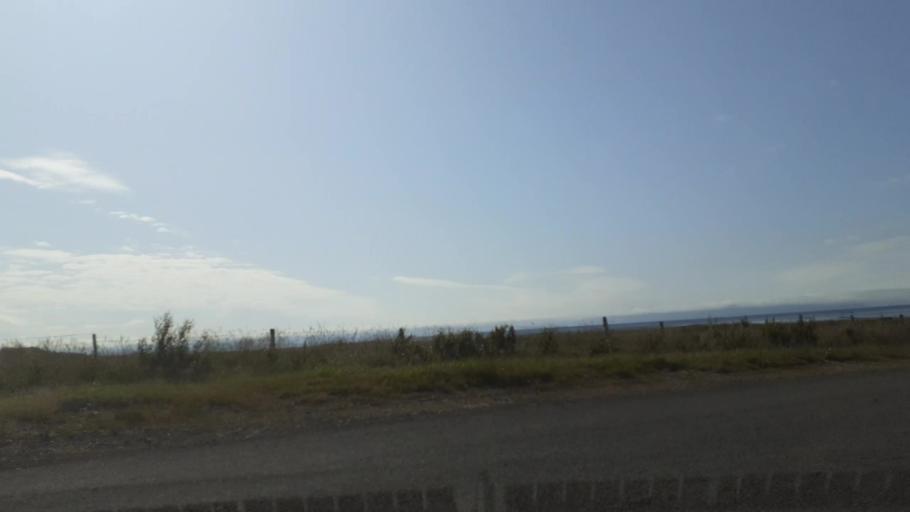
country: IS
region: Northwest
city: Saudarkrokur
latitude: 65.8207
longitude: -20.2995
